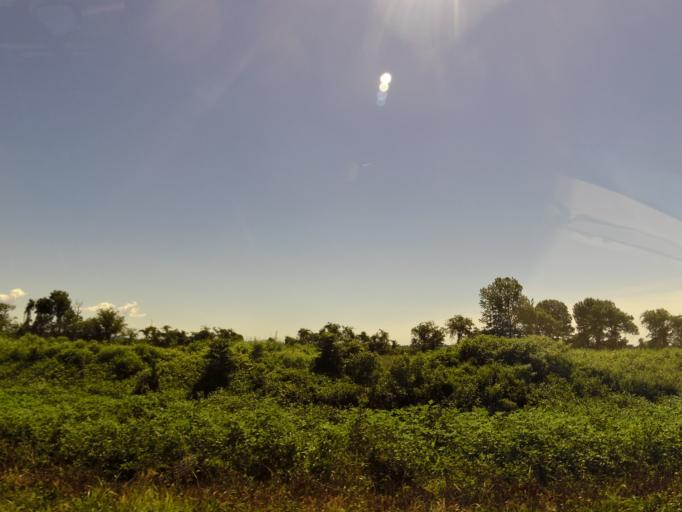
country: US
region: Missouri
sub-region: New Madrid County
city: Lilbourn
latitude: 36.5642
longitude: -89.7027
